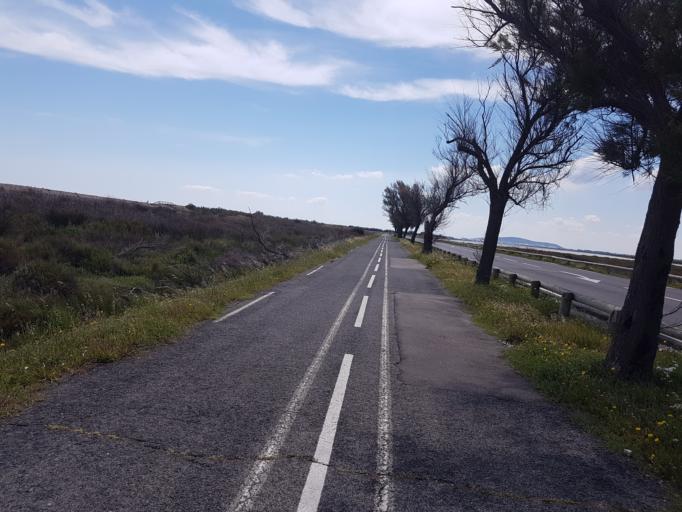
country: FR
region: Languedoc-Roussillon
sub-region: Departement de l'Herault
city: Vic-la-Gardiole
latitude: 43.4595
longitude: 3.8180
